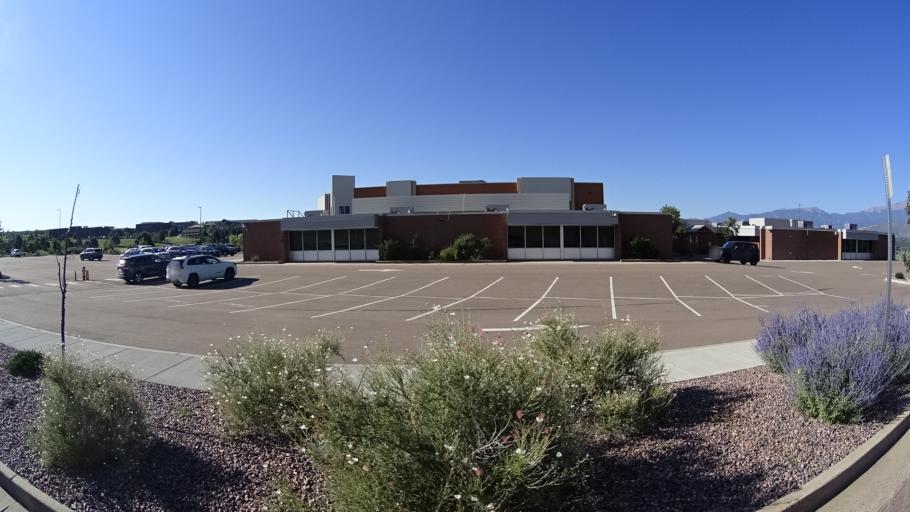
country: US
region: Colorado
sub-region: El Paso County
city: Air Force Academy
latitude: 38.9693
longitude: -104.7951
